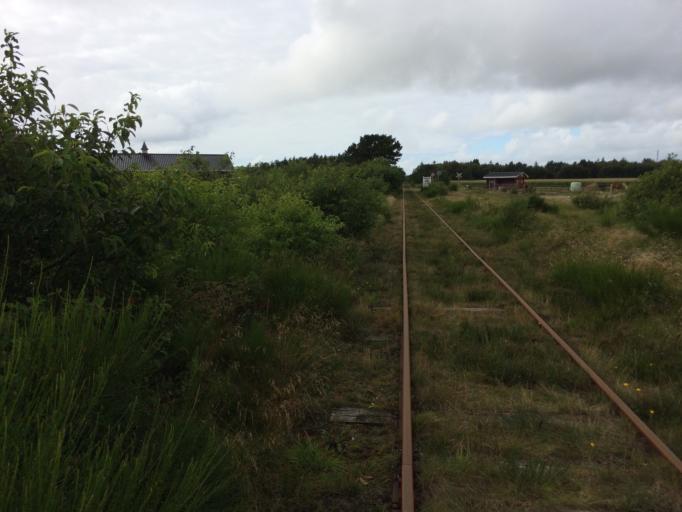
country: DK
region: South Denmark
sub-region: Varde Kommune
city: Oksbol
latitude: 55.8082
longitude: 8.2111
